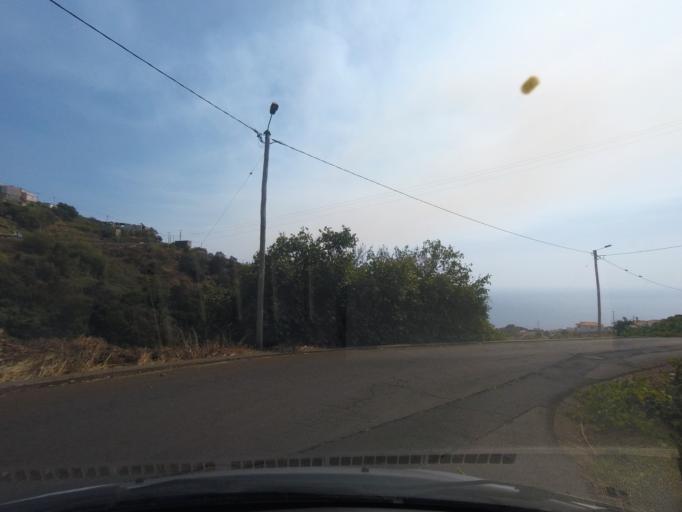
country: PT
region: Madeira
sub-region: Ribeira Brava
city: Campanario
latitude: 32.6865
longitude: -17.0635
